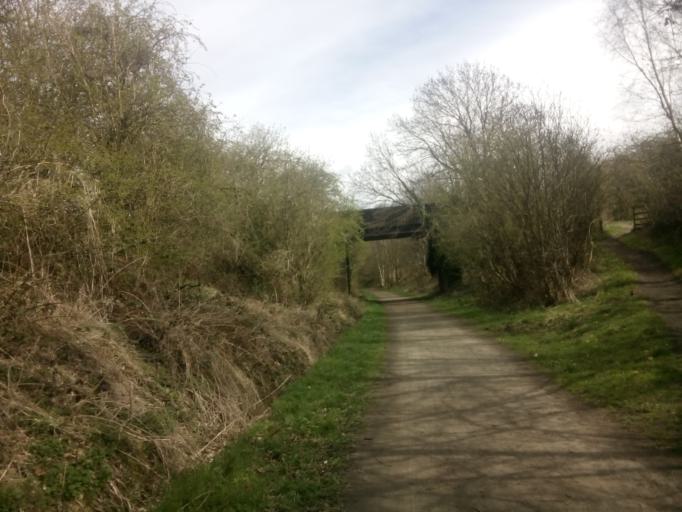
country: GB
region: England
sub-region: County Durham
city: Ushaw Moor
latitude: 54.7672
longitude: -1.6211
